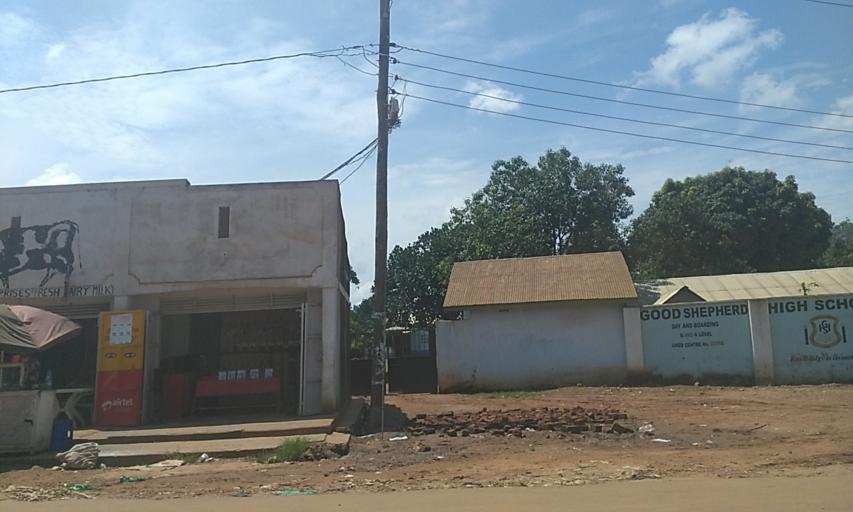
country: UG
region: Central Region
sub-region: Wakiso District
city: Wakiso
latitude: 0.3833
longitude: 32.5180
